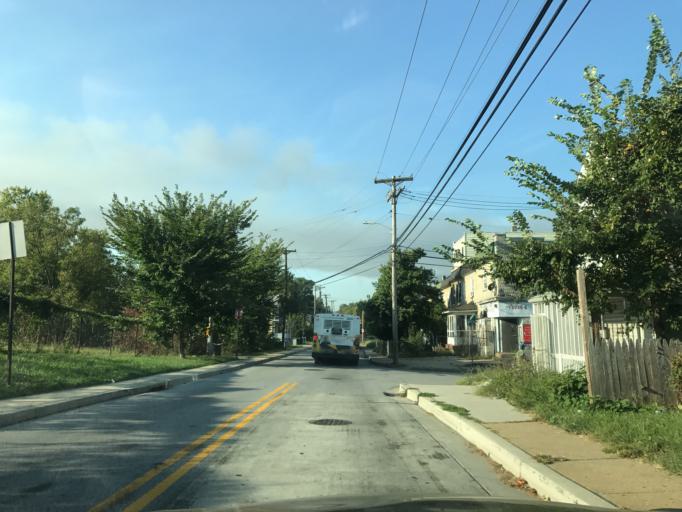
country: US
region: Maryland
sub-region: Baltimore County
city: Lansdowne
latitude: 39.2606
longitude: -76.6424
